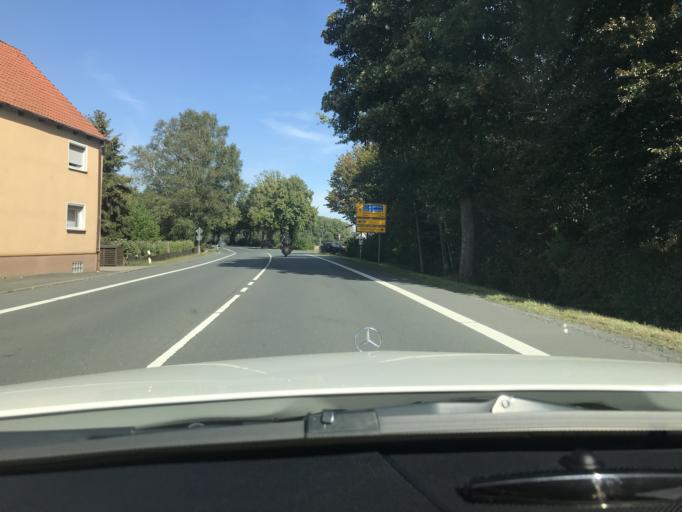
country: DE
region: North Rhine-Westphalia
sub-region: Regierungsbezirk Arnsberg
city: Bonen
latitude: 51.6032
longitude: 7.7955
